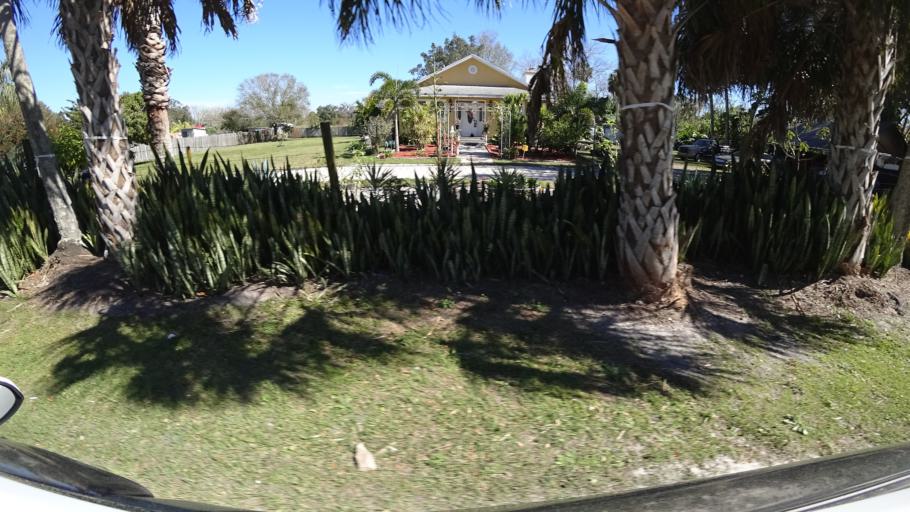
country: US
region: Florida
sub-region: Manatee County
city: Memphis
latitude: 27.5563
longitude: -82.5482
